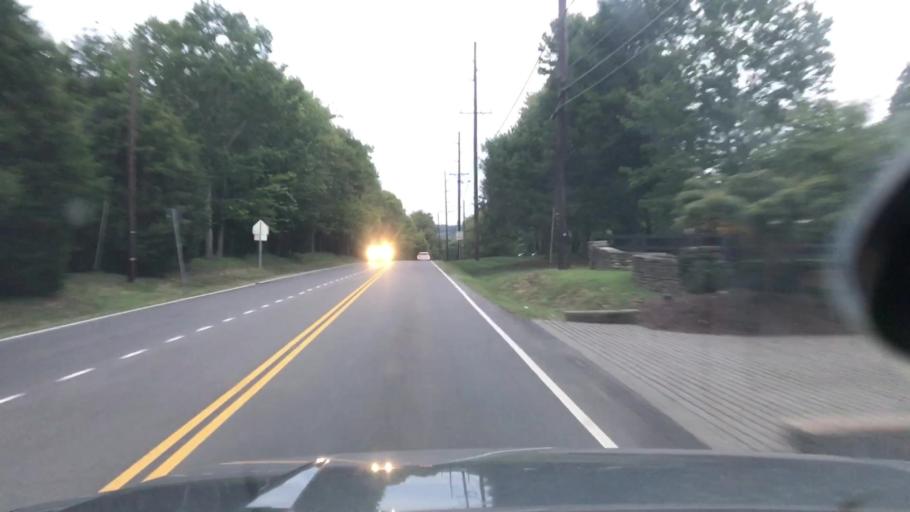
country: US
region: Tennessee
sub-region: Davidson County
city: Forest Hills
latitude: 36.0492
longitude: -86.8712
